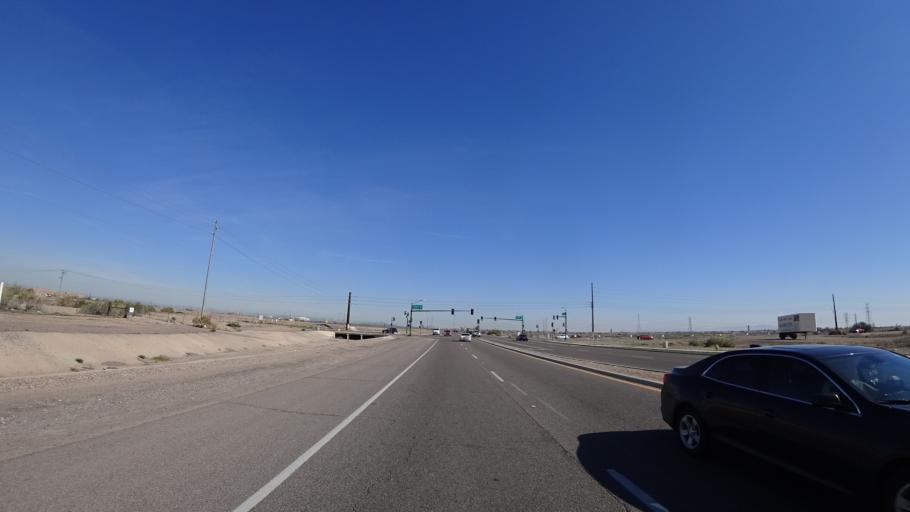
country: US
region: Arizona
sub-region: Maricopa County
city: Litchfield Park
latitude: 33.5076
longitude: -112.3250
